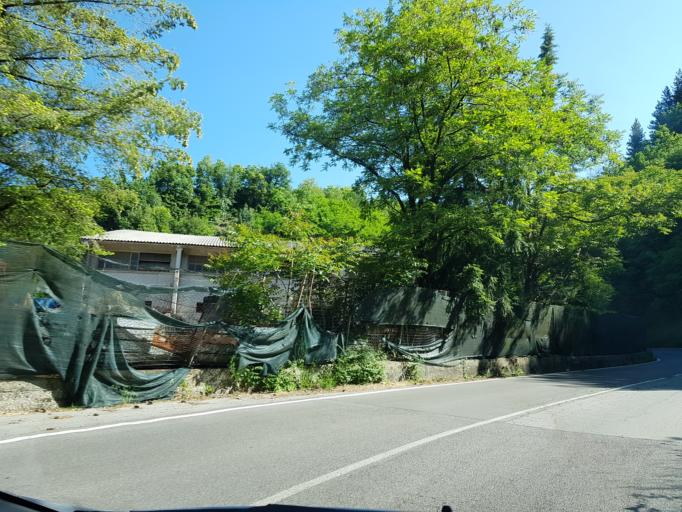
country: IT
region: Tuscany
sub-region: Provincia di Lucca
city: Piazza al Serchio-San Michele
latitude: 44.1764
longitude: 10.3136
